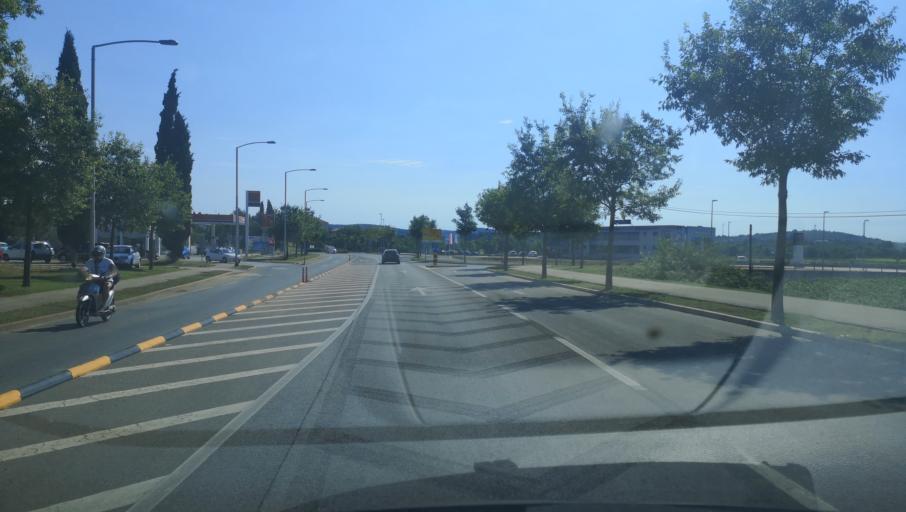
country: HR
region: Istarska
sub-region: Grad Rovinj
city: Rovinj
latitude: 45.0790
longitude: 13.6610
